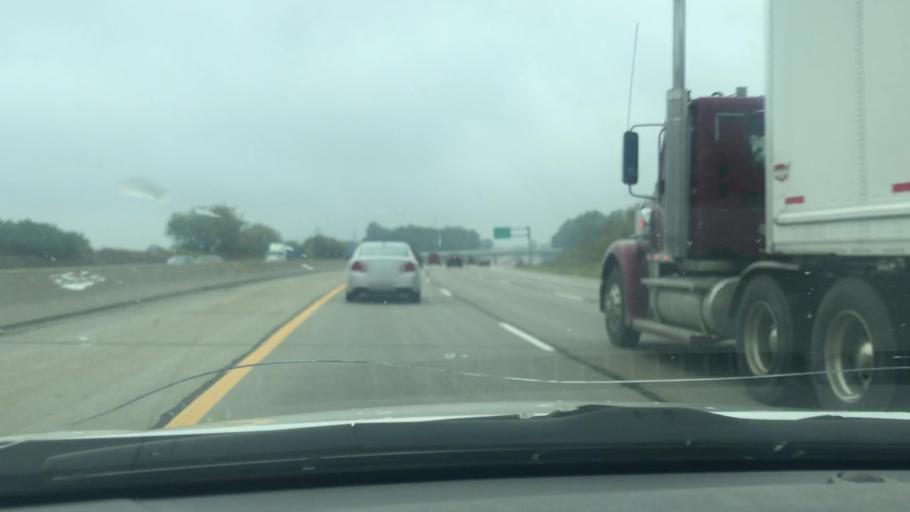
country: US
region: Michigan
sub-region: Livingston County
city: Howell
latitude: 42.5834
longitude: -83.9016
